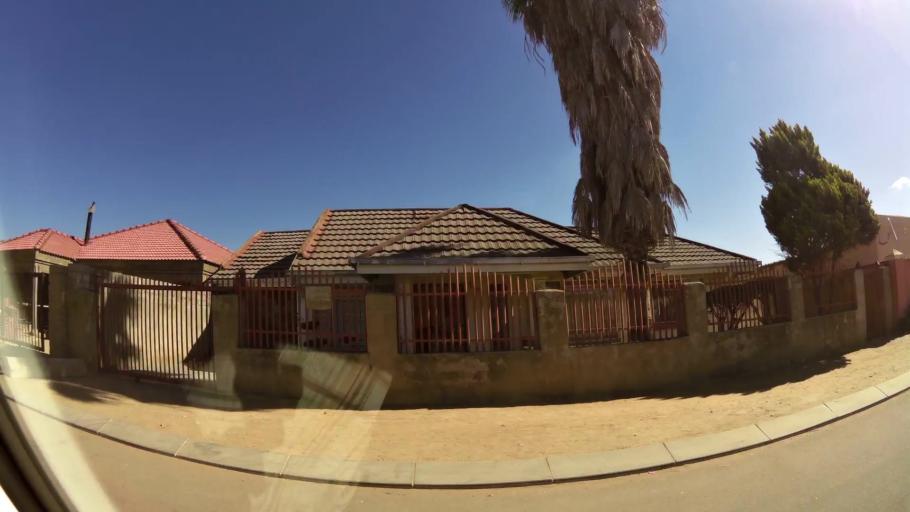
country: ZA
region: Limpopo
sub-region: Capricorn District Municipality
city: Polokwane
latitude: -23.8526
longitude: 29.4089
